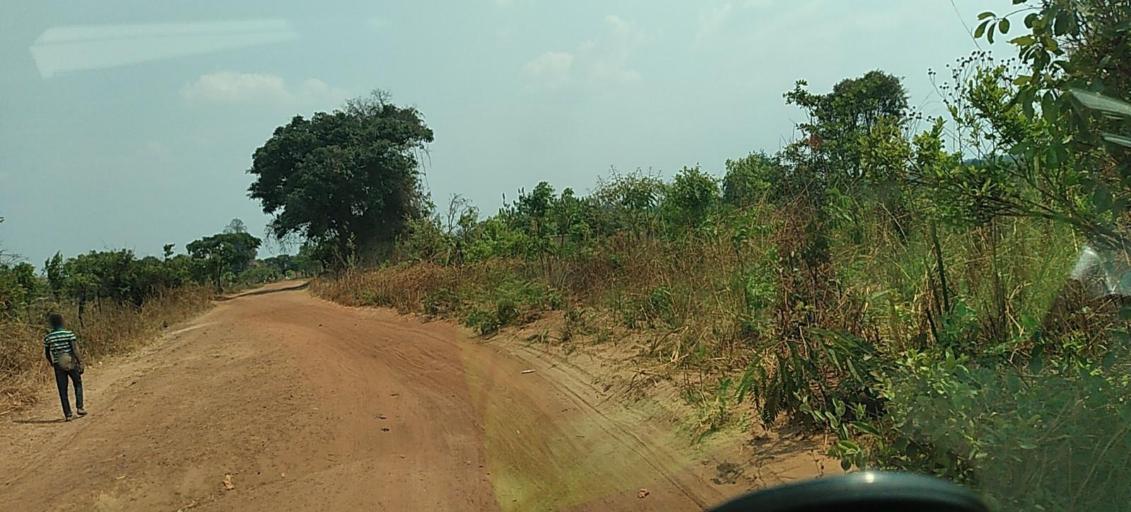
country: ZM
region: North-Western
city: Kansanshi
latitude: -12.0950
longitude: 26.3633
